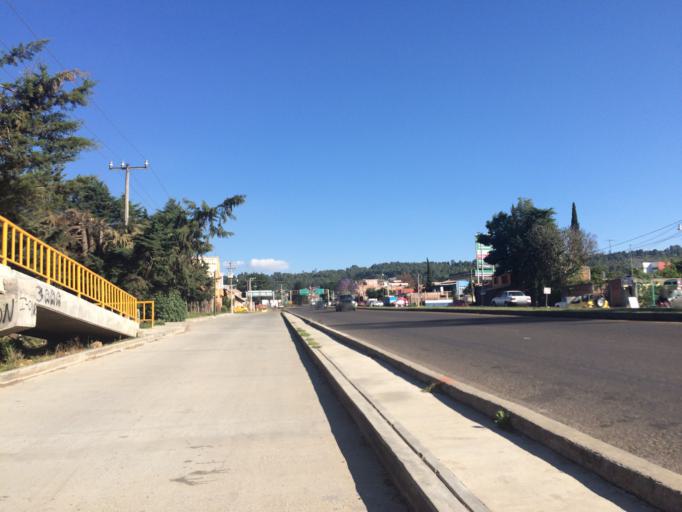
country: MX
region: Michoacan
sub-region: Patzcuaro
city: Colonia Vista Bella (Lomas del Peaje)
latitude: 19.4984
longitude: -101.6003
